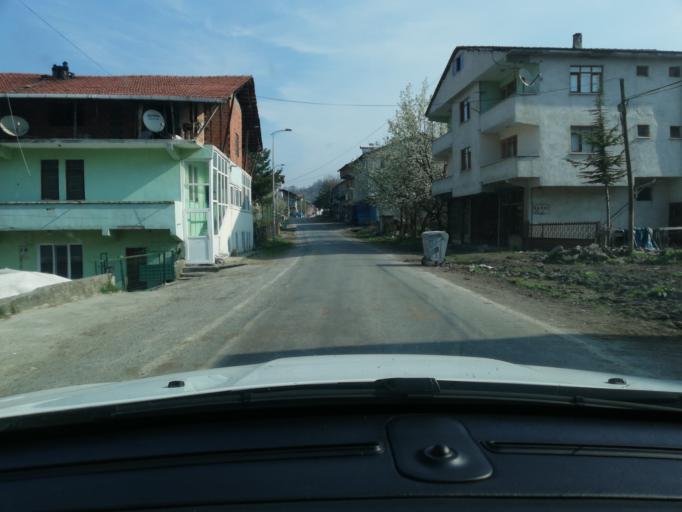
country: TR
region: Karabuk
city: Yenice
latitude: 41.2591
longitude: 32.3624
